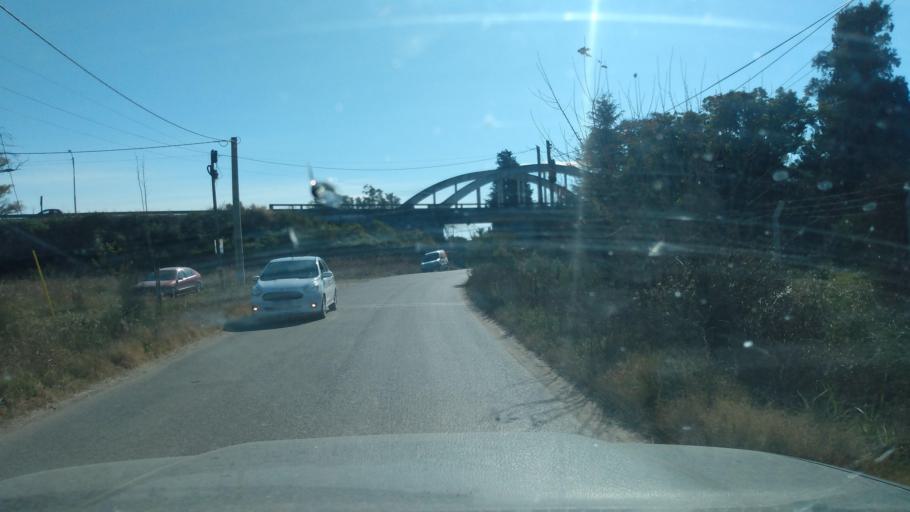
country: AR
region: Buenos Aires
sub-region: Partido de Lujan
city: Lujan
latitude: -34.5780
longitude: -59.0890
